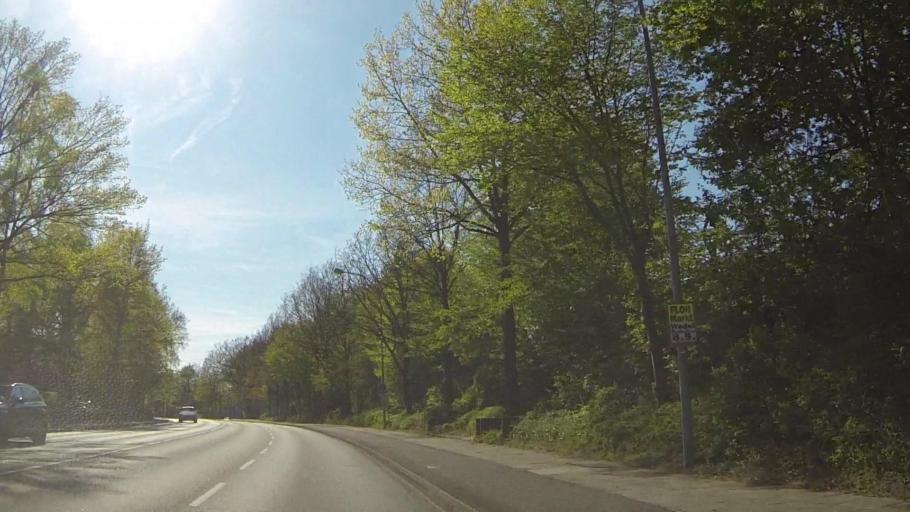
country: DE
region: Schleswig-Holstein
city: Rellingen
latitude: 53.6450
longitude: 9.8080
